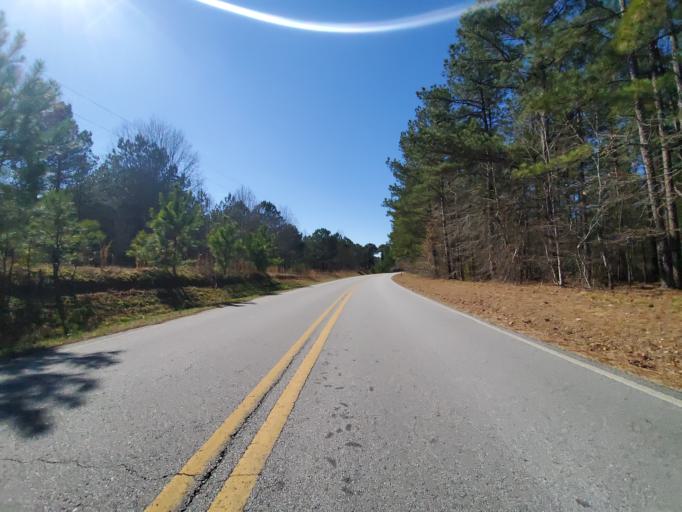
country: US
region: Georgia
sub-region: Gwinnett County
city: Dacula
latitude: 33.9755
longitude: -83.8652
